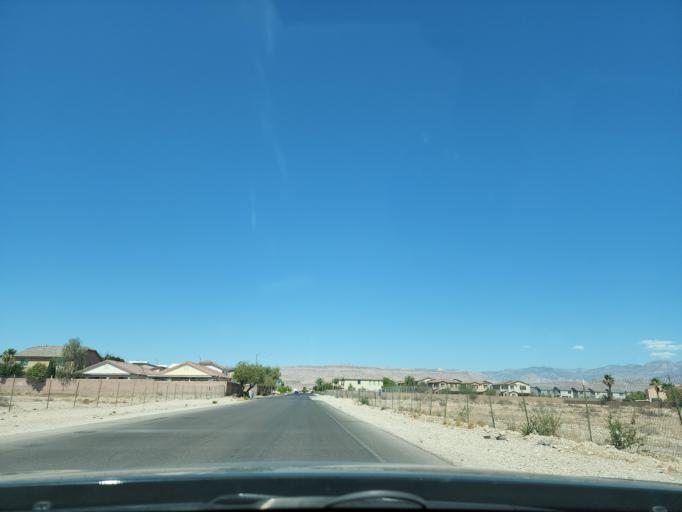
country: US
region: Nevada
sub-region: Clark County
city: Spring Valley
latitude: 36.0813
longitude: -115.2565
